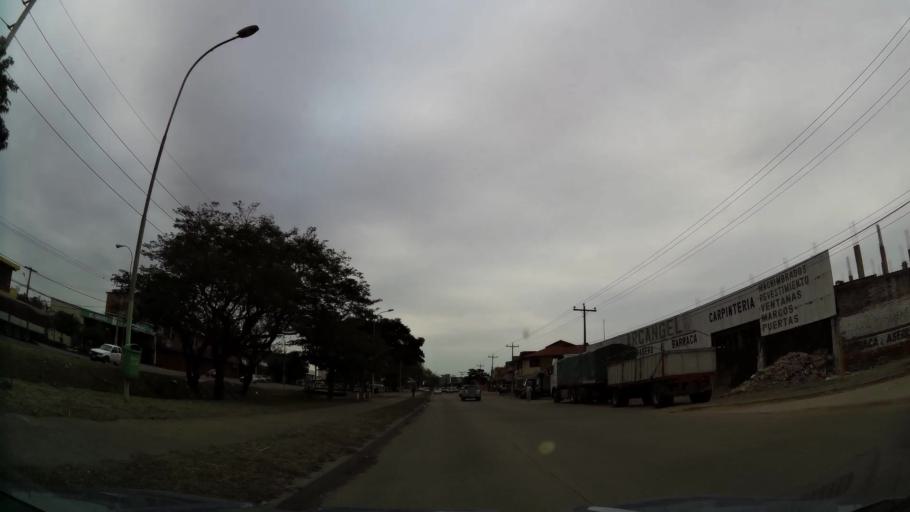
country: BO
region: Santa Cruz
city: Santa Cruz de la Sierra
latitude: -17.8006
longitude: -63.1506
